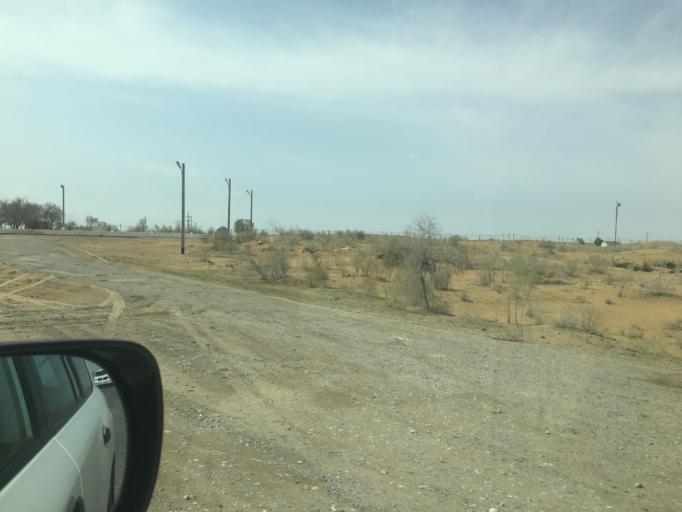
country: TM
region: Mary
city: Seydi
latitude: 39.7708
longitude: 62.5339
